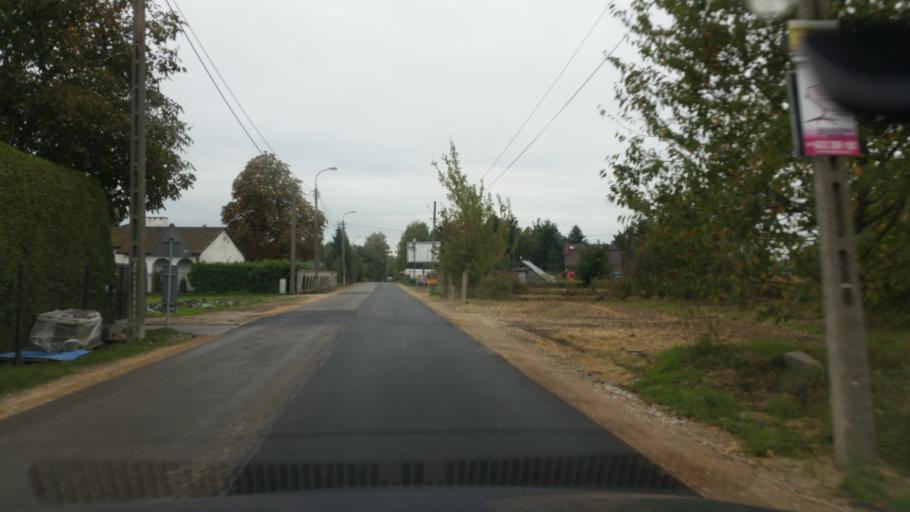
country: PL
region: Masovian Voivodeship
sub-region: Powiat piaseczynski
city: Jozefoslaw
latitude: 52.0956
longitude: 21.0783
